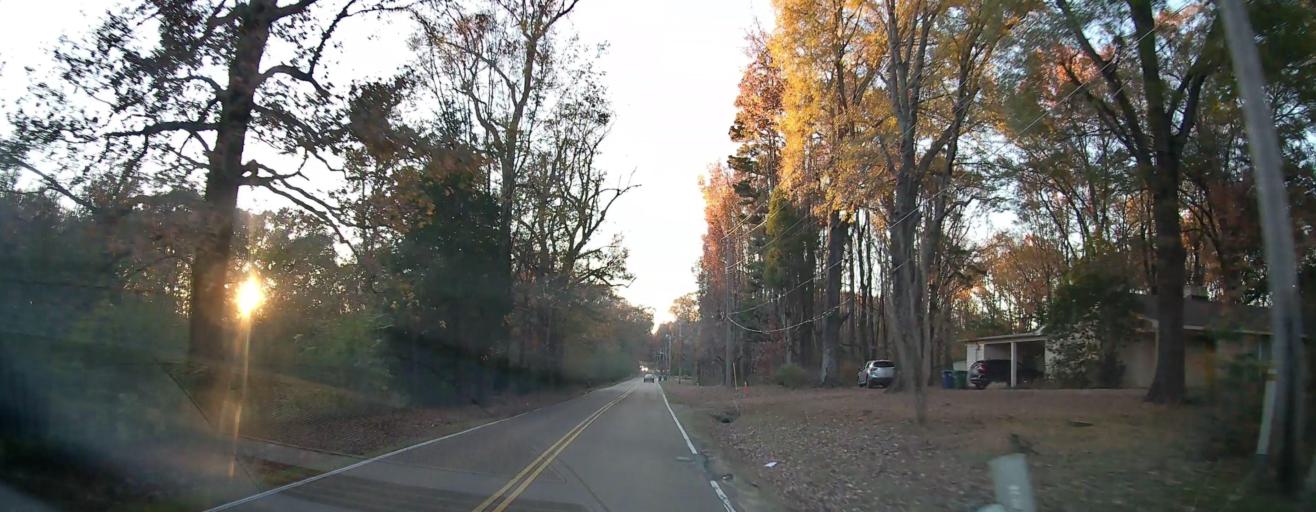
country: US
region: Tennessee
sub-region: Shelby County
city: Germantown
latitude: 35.0775
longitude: -89.8195
